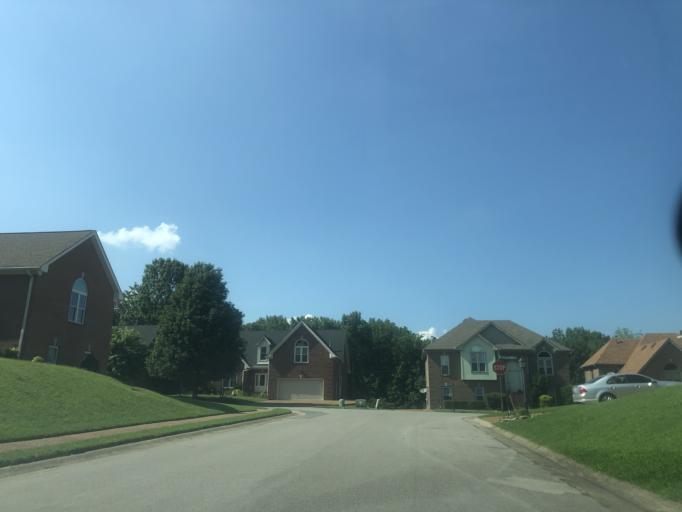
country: US
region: Tennessee
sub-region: Wilson County
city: Green Hill
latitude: 36.1528
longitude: -86.5930
